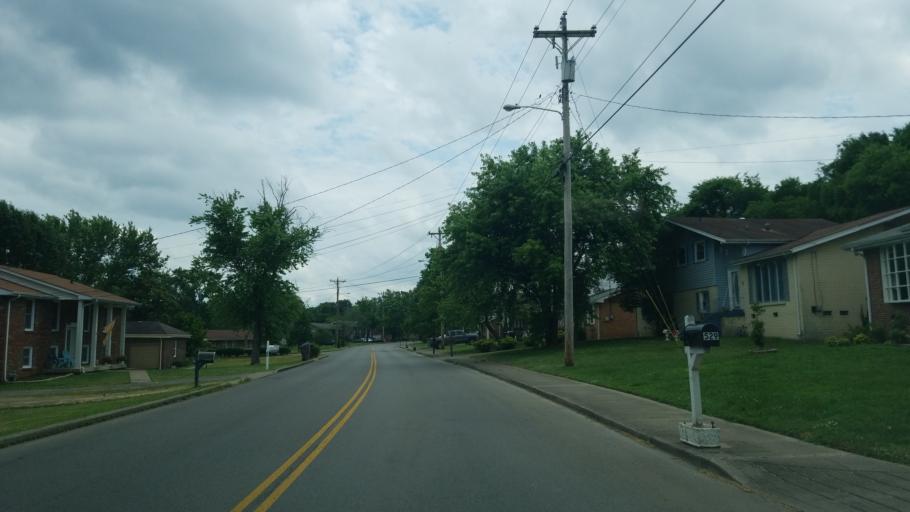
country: US
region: Tennessee
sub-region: Rutherford County
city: La Vergne
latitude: 36.0841
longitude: -86.6235
